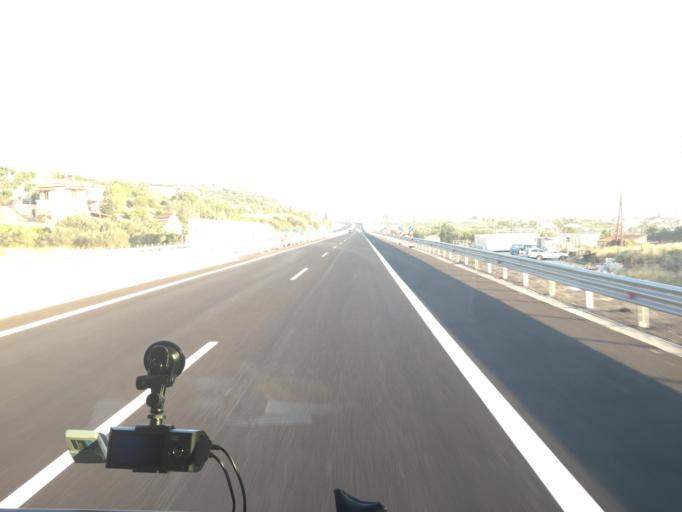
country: GR
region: Peloponnese
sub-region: Nomos Korinthias
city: Xylokastro
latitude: 38.0865
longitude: 22.5801
